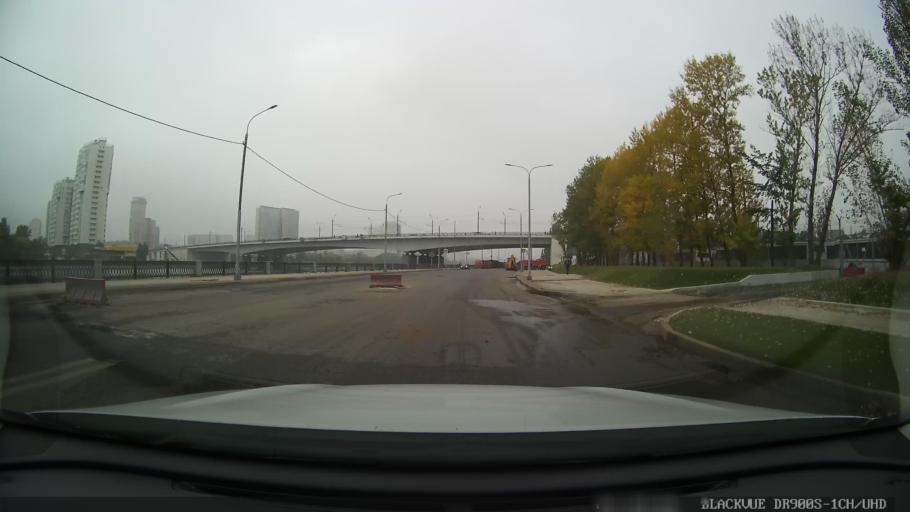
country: RU
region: Moskovskaya
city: Kozhukhovo
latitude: 55.6869
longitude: 37.6687
